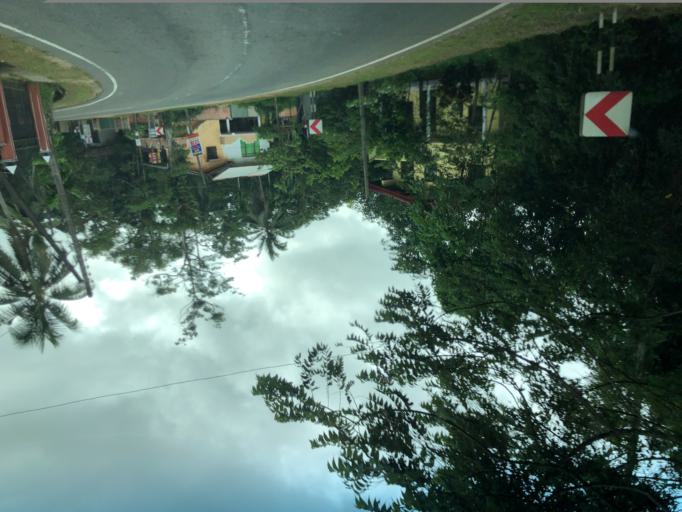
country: LK
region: Western
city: Horana South
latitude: 6.6817
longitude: 80.0955
